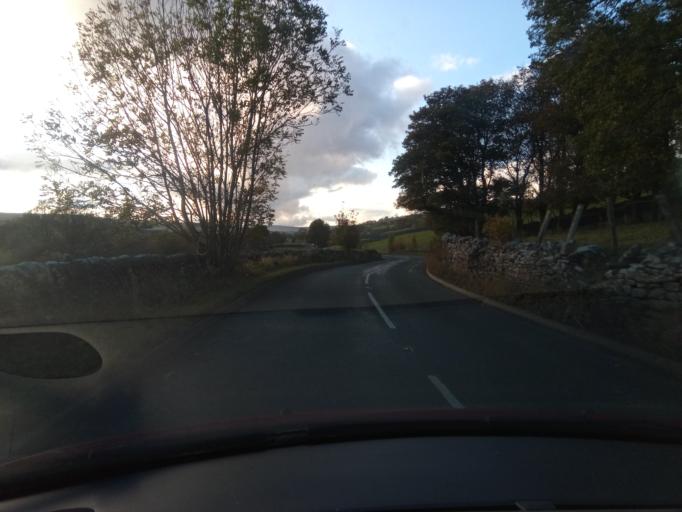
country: GB
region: England
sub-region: County Durham
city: Newbiggin
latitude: 54.7378
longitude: -2.1301
